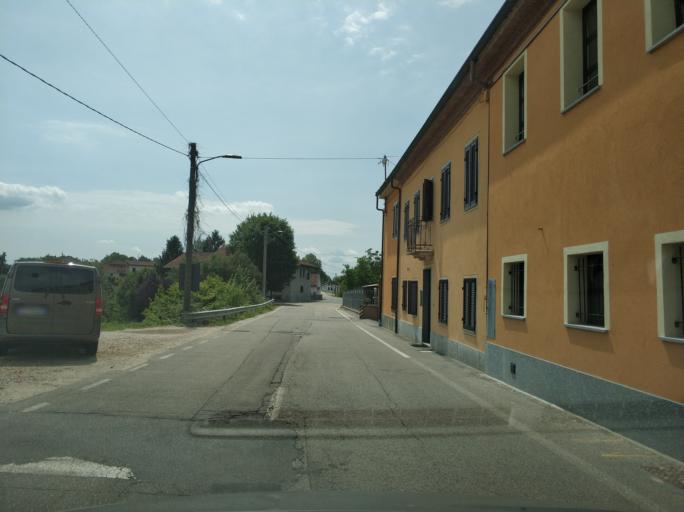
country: IT
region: Piedmont
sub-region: Provincia di Cuneo
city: Santo Stefano Roero
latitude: 44.7871
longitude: 7.9428
